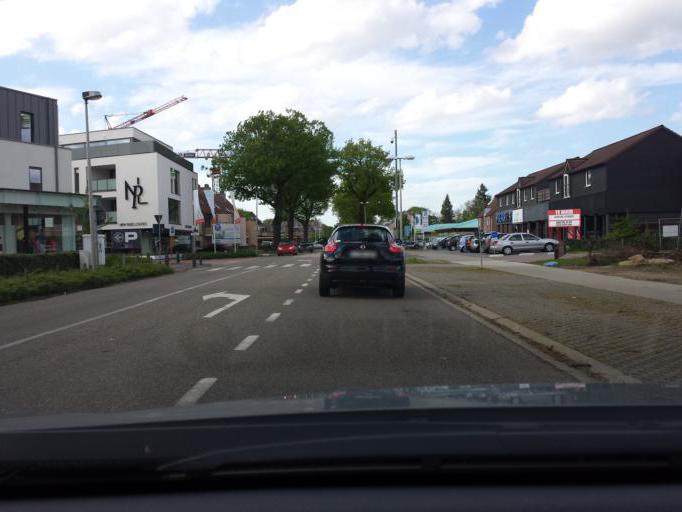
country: BE
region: Flanders
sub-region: Provincie Limburg
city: Maasmechelen
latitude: 50.9856
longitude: 5.6996
